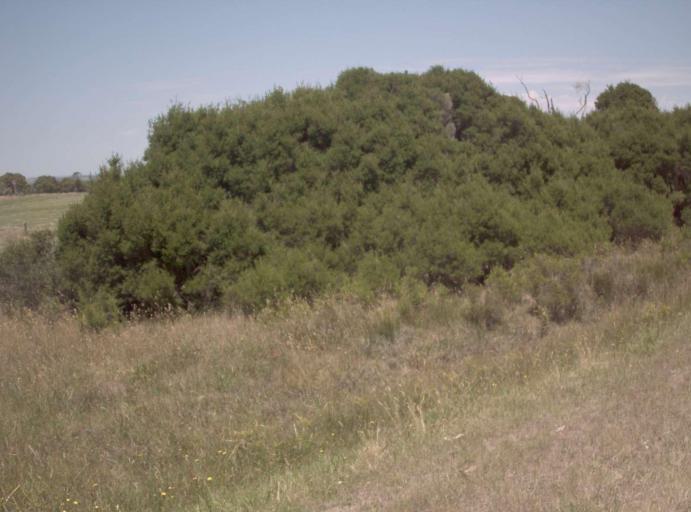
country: AU
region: Victoria
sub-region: Bass Coast
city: North Wonthaggi
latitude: -38.6667
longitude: 145.9256
